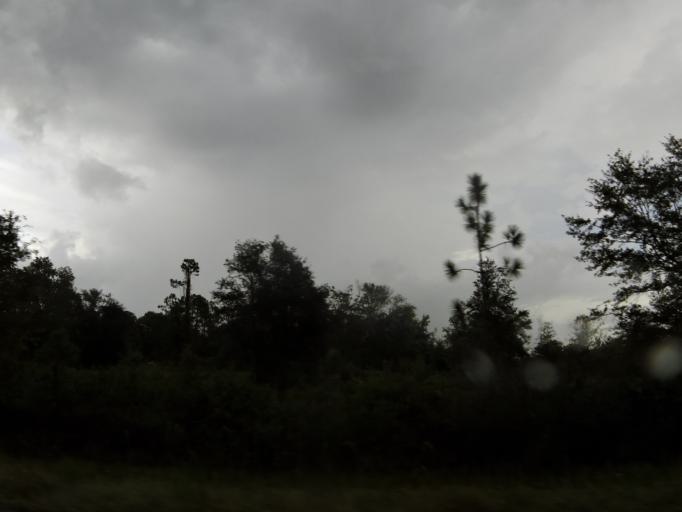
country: US
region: Florida
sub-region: Nassau County
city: Hilliard
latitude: 30.5397
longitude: -82.0398
